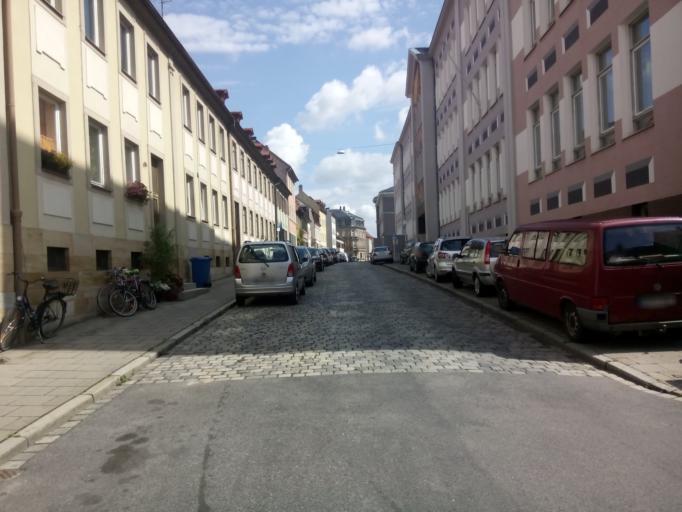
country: DE
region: Bavaria
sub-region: Upper Franconia
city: Bamberg
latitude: 49.8941
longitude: 10.8834
